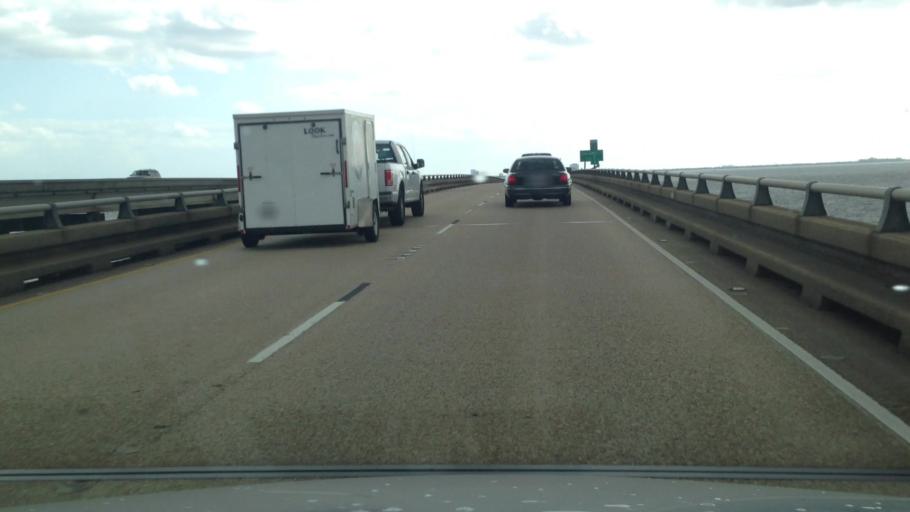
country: US
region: Louisiana
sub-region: Jefferson Parish
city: Metairie
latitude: 30.0782
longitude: -90.1444
